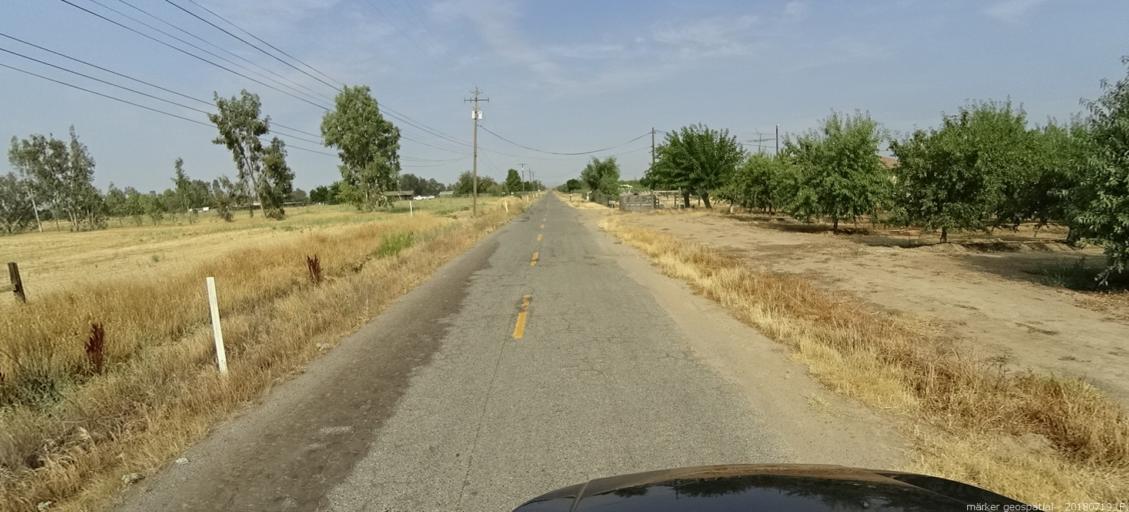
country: US
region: California
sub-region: Madera County
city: Fairmead
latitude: 37.0910
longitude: -120.1858
